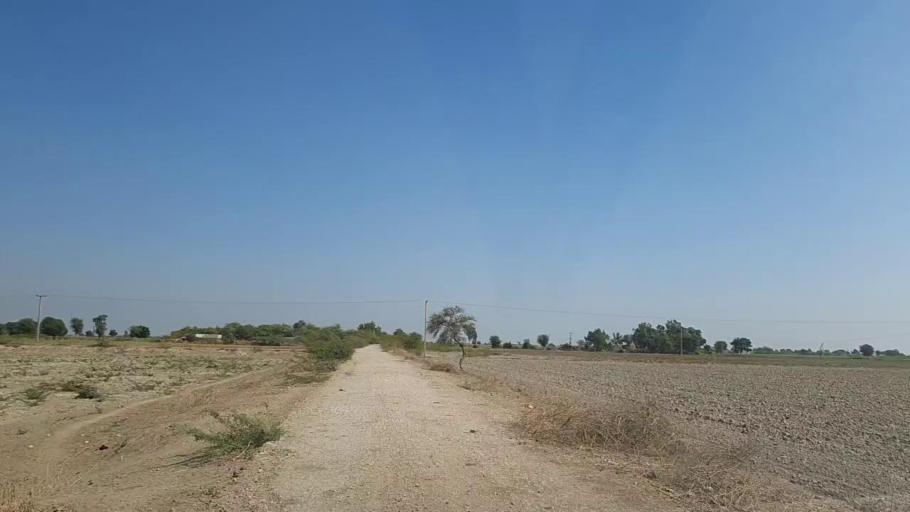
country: PK
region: Sindh
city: Pithoro
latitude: 25.4108
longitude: 69.4066
